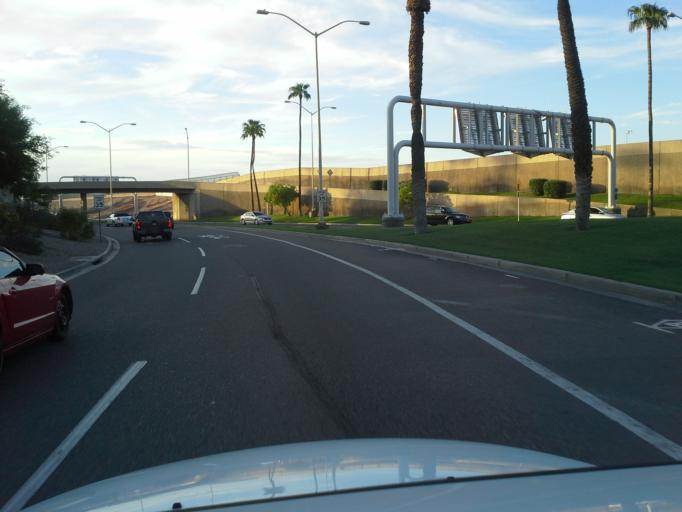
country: US
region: Arizona
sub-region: Maricopa County
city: Phoenix
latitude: 33.4357
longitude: -112.0105
